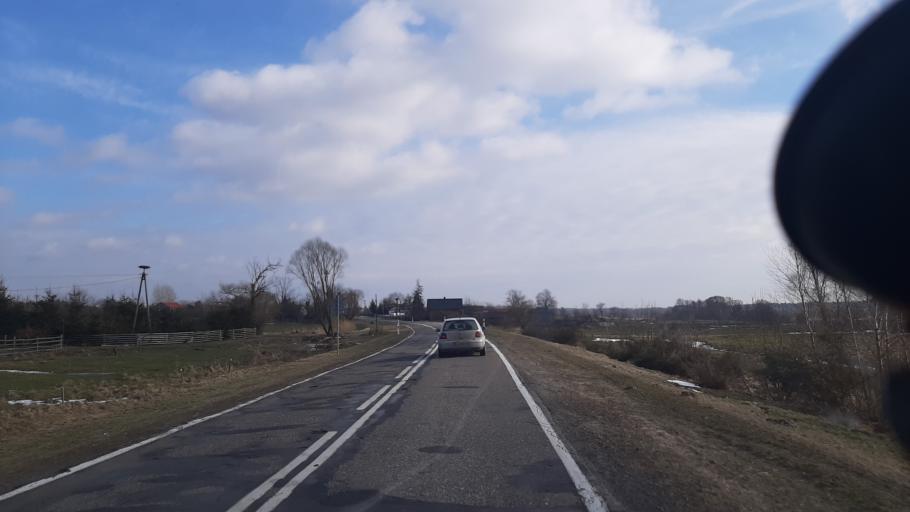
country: PL
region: Lublin Voivodeship
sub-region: Powiat parczewski
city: Sosnowica
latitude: 51.5006
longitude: 23.1459
